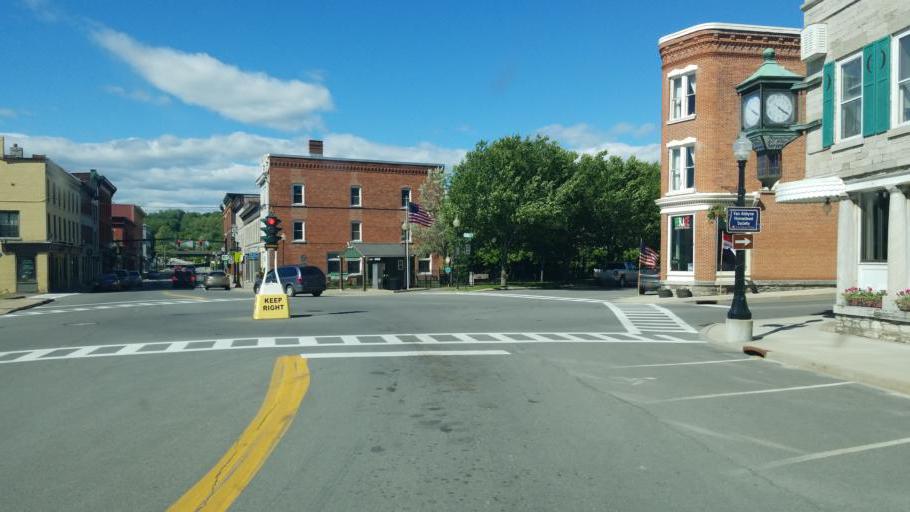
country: US
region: New York
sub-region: Montgomery County
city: Canajoharie
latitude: 42.9050
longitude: -74.5722
